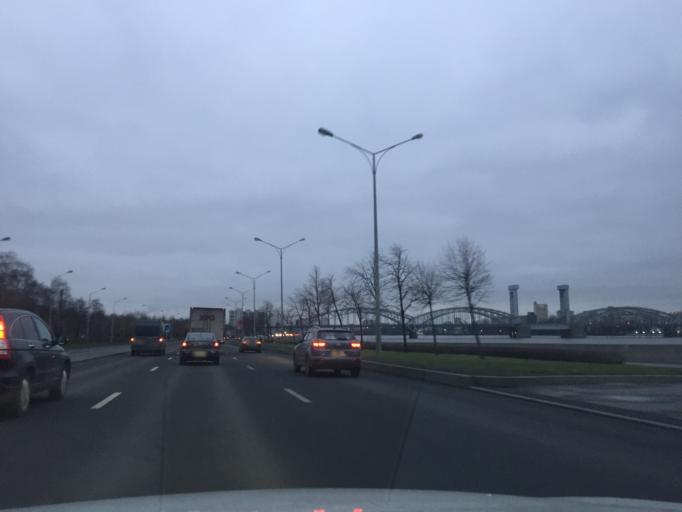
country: RU
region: St.-Petersburg
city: Centralniy
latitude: 59.9210
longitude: 30.4081
